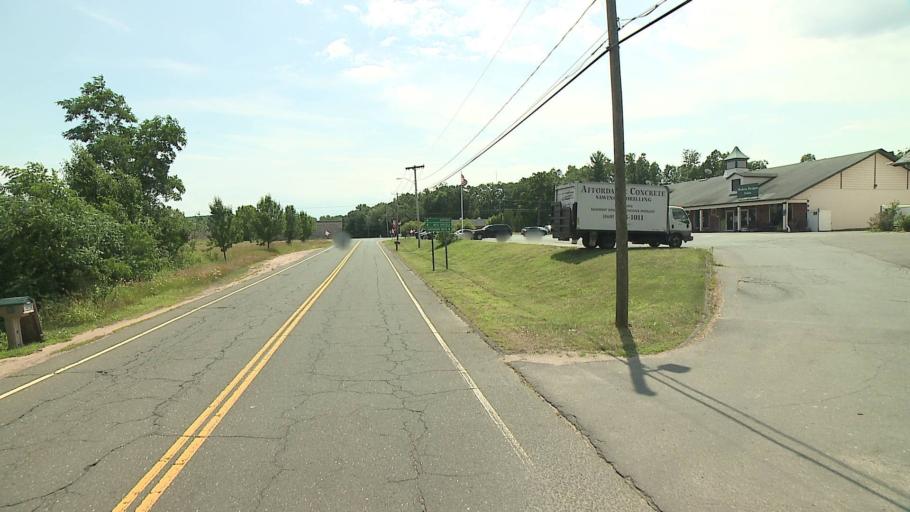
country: US
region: Massachusetts
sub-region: Hampden County
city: Southwick
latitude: 42.0199
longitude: -72.7481
